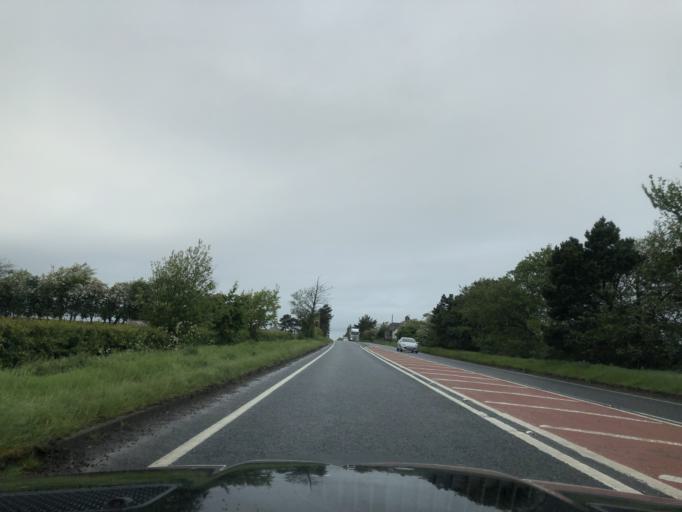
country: GB
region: Northern Ireland
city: Dunloy
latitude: 55.0331
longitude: -6.4029
